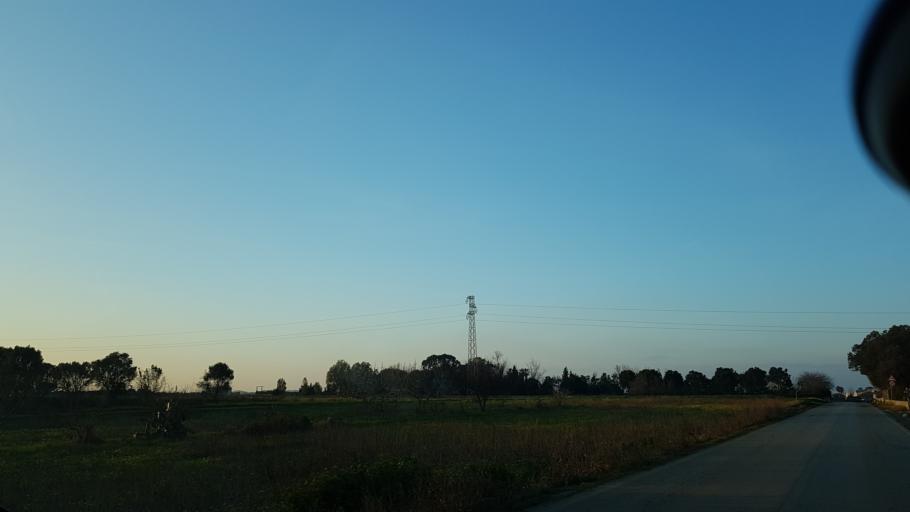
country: IT
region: Apulia
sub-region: Provincia di Brindisi
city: La Rosa
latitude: 40.6016
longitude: 17.9463
